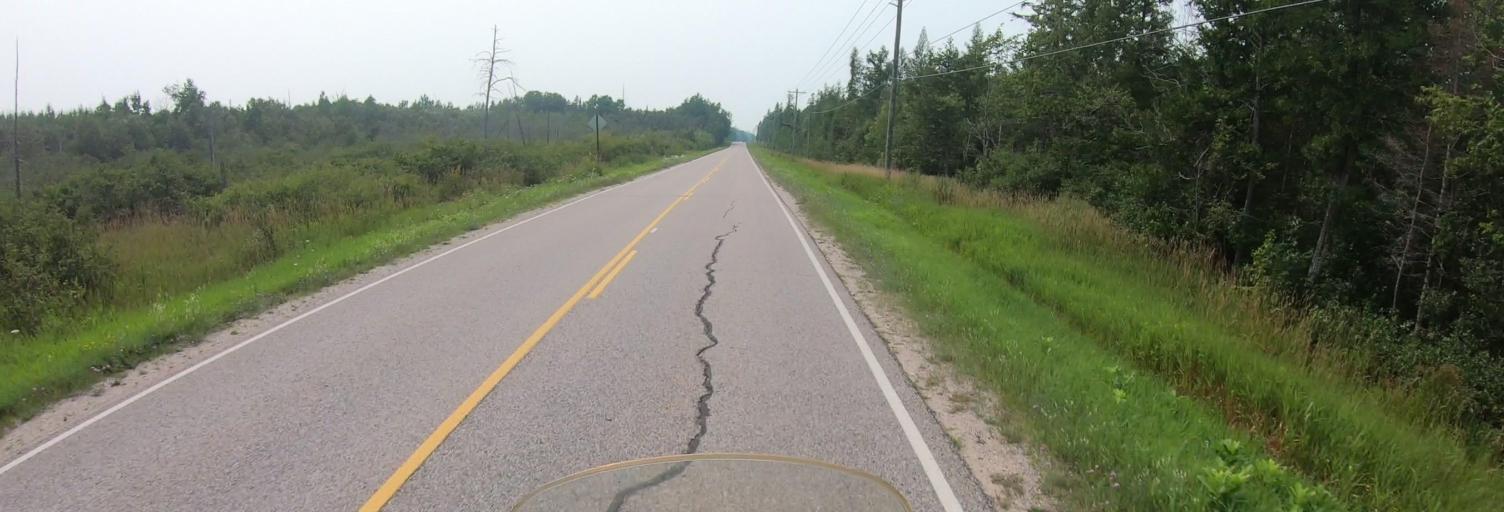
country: CA
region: Ontario
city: Thessalon
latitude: 46.0149
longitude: -84.0311
